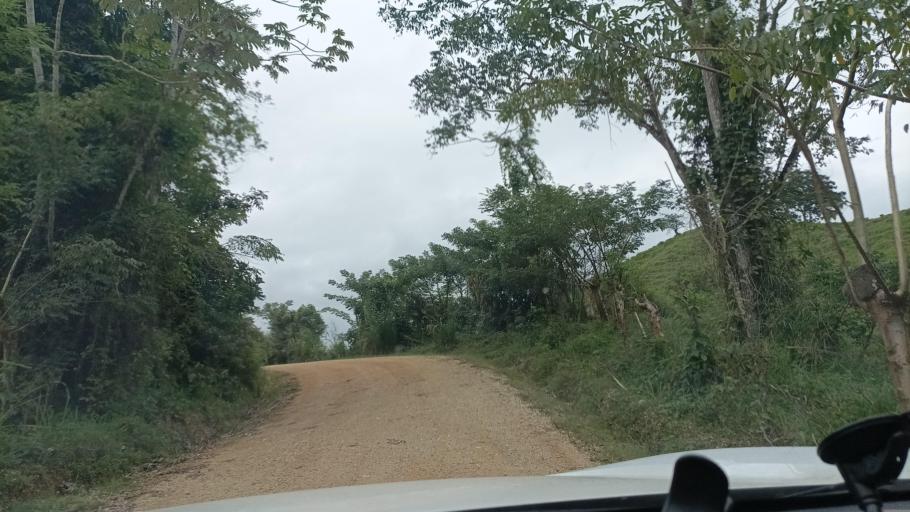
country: MX
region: Veracruz
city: Hidalgotitlan
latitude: 17.6197
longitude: -94.5157
